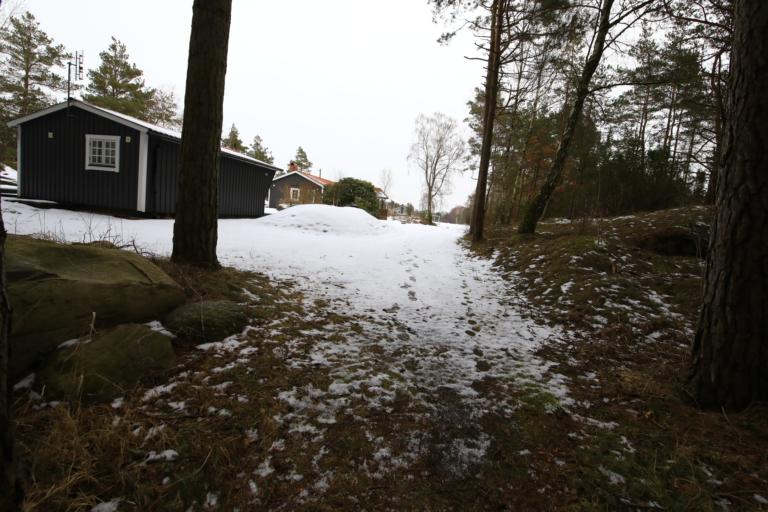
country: SE
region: Halland
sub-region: Kungsbacka Kommun
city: Frillesas
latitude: 57.2164
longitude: 12.1464
